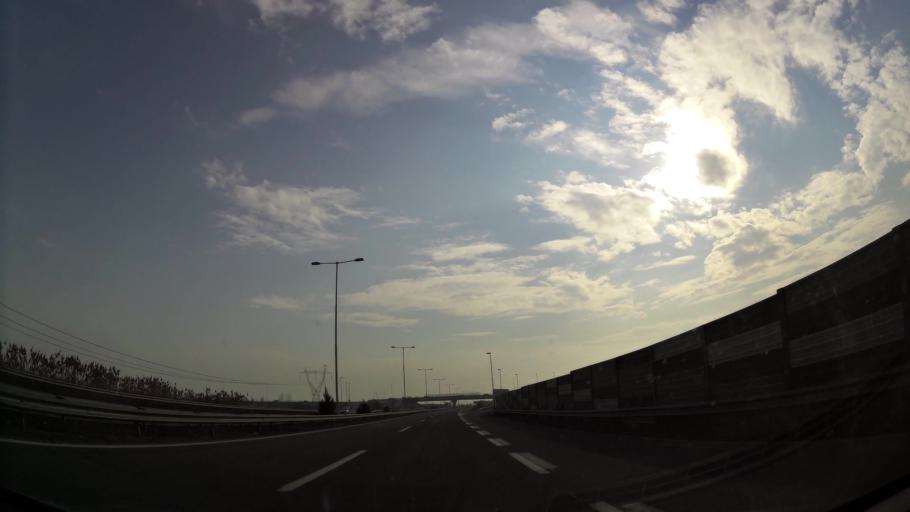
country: MK
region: Aracinovo
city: Arachinovo
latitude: 42.0203
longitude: 21.5332
